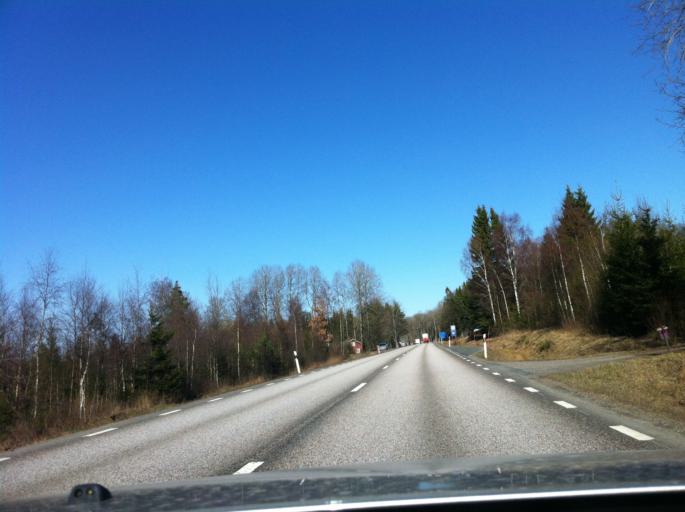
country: SE
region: Joenkoeping
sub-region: Mullsjo Kommun
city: Mullsjoe
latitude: 58.0272
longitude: 13.8333
